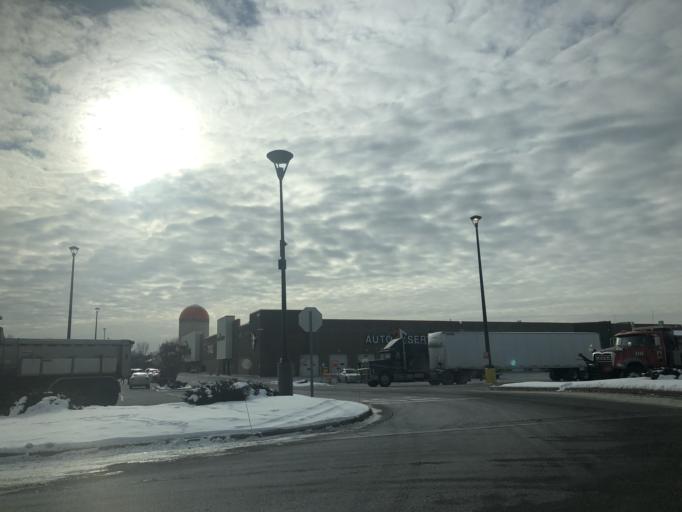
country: US
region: Minnesota
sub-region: Anoka County
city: Lexington
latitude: 45.1567
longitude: -93.1653
